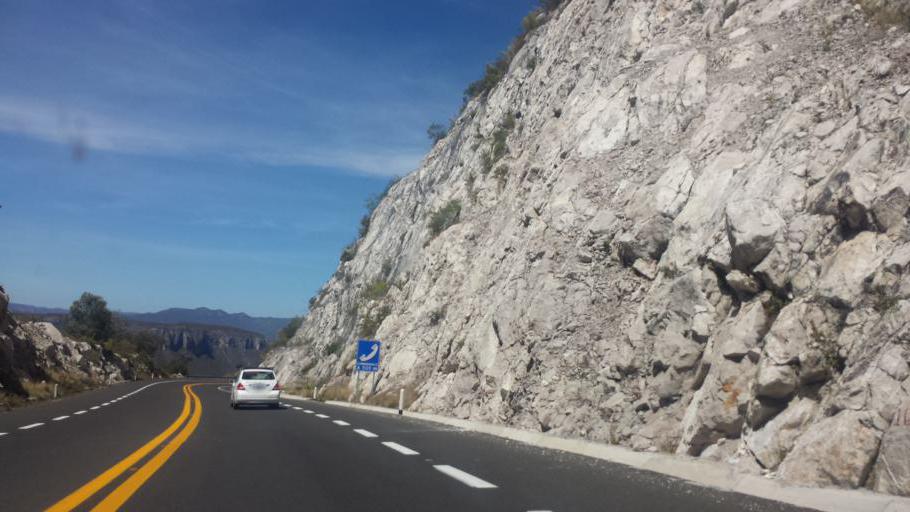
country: MX
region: Puebla
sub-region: San Jose Miahuatlan
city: San Pedro Tetitlan
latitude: 18.0280
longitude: -97.3477
